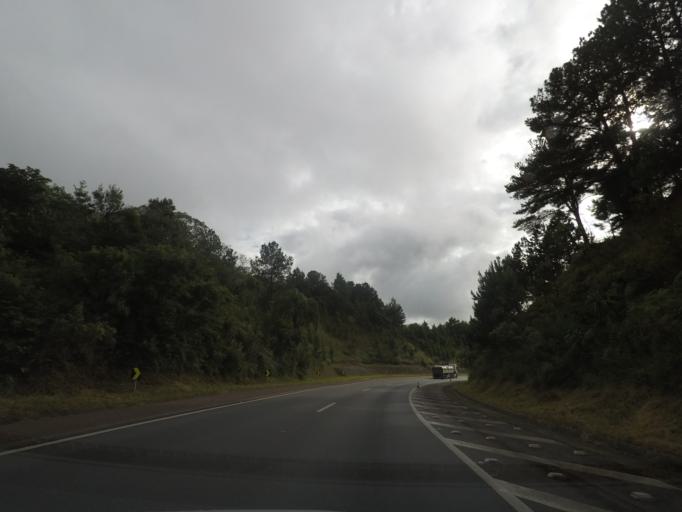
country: BR
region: Parana
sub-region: Campina Grande Do Sul
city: Campina Grande do Sul
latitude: -25.1859
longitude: -48.8850
